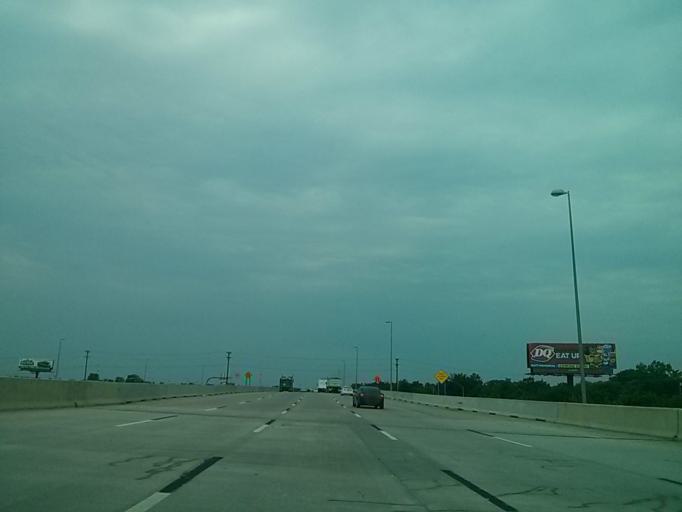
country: US
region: Oklahoma
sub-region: Tulsa County
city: Owasso
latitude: 36.1650
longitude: -95.8664
